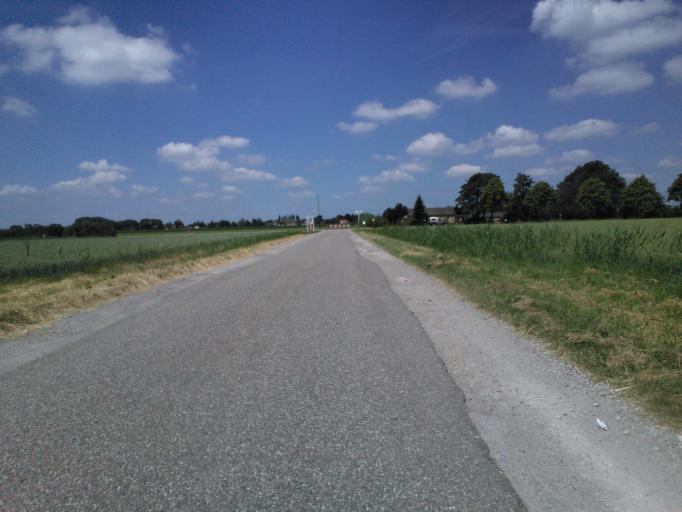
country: NL
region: North Brabant
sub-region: Gemeente Woudrichem
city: Woudrichem
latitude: 51.8010
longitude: 4.9853
